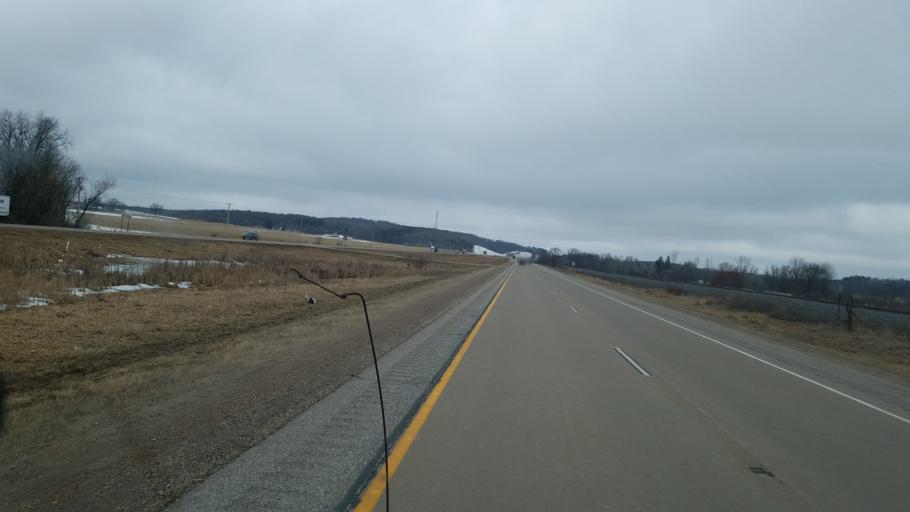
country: US
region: Wisconsin
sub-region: Portage County
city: Amherst
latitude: 44.4033
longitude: -89.2220
